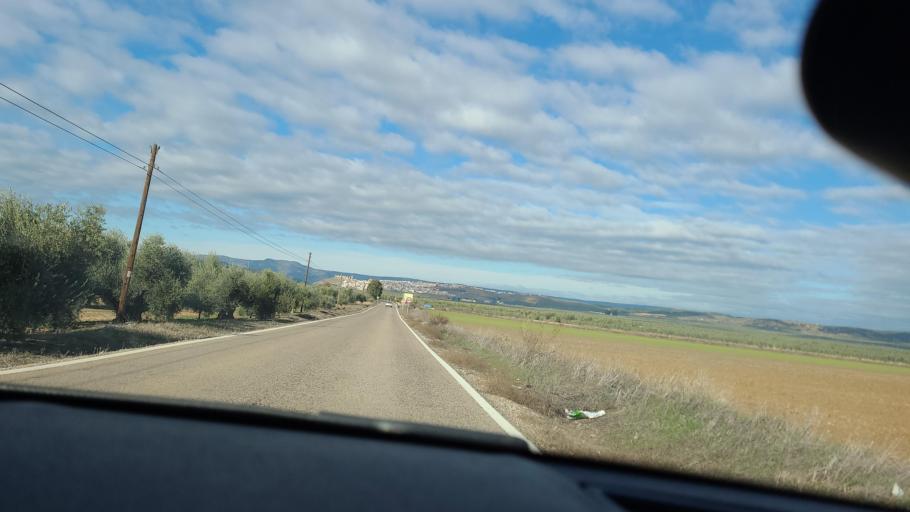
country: ES
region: Andalusia
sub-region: Provincia de Jaen
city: Banos de la Encina
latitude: 38.1495
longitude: -3.7385
